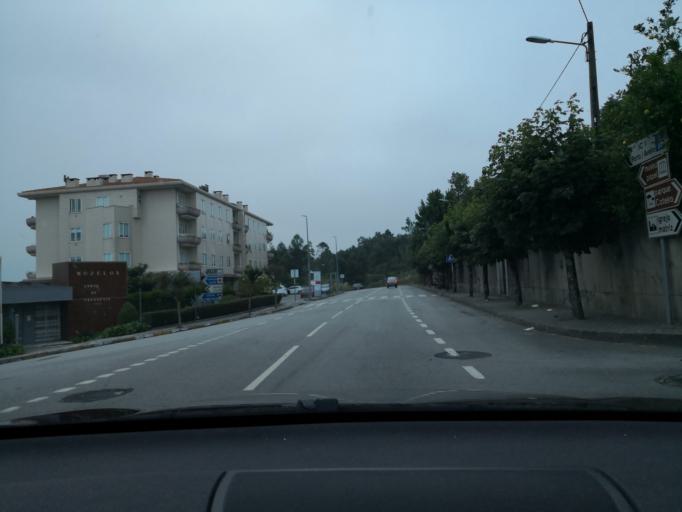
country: PT
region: Aveiro
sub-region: Santa Maria da Feira
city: Lamas
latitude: 40.9993
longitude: -8.5664
